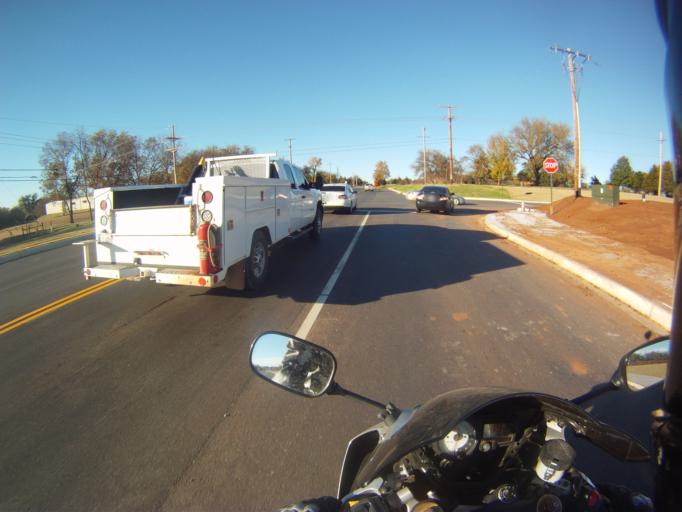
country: US
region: Oklahoma
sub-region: Payne County
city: Stillwater
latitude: 36.1299
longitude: -97.1230
